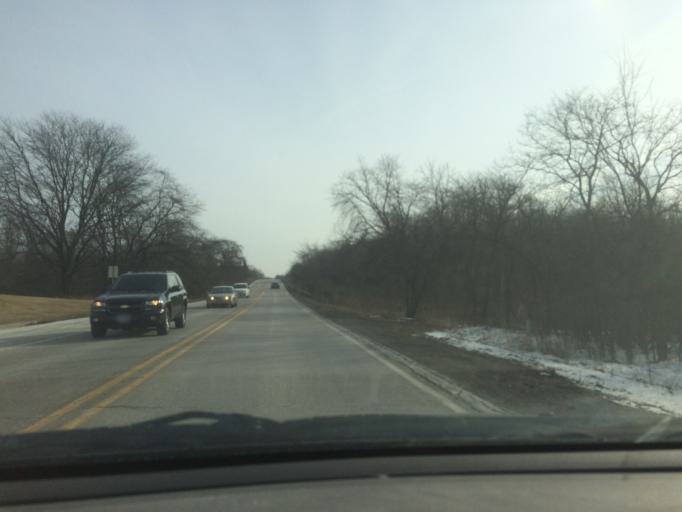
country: US
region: Illinois
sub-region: Cook County
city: Streamwood
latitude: 42.0463
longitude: -88.1652
